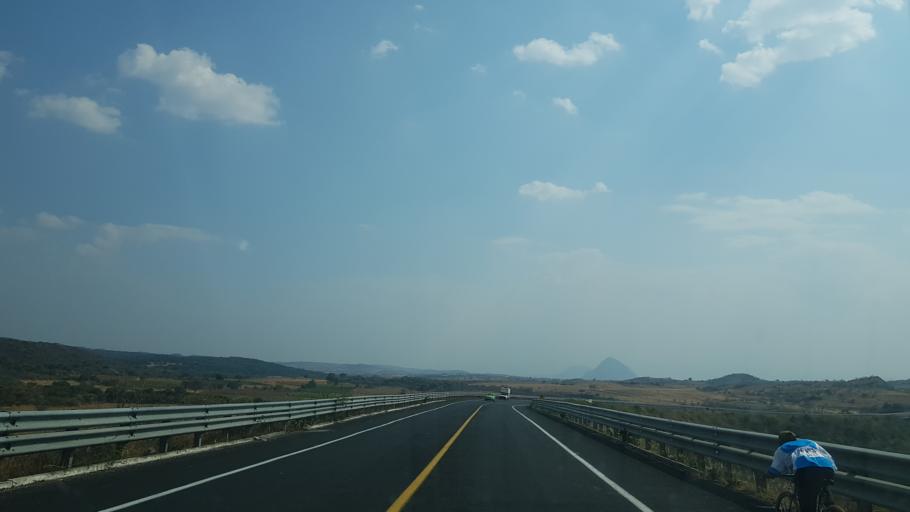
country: MX
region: Puebla
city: San Juan Amecac
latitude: 18.8160
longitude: -98.6953
